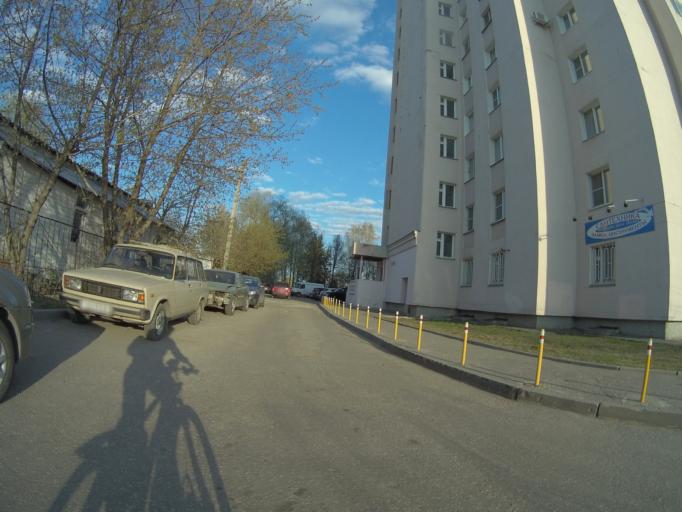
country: RU
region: Vladimir
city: Vladimir
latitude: 56.1422
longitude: 40.3644
